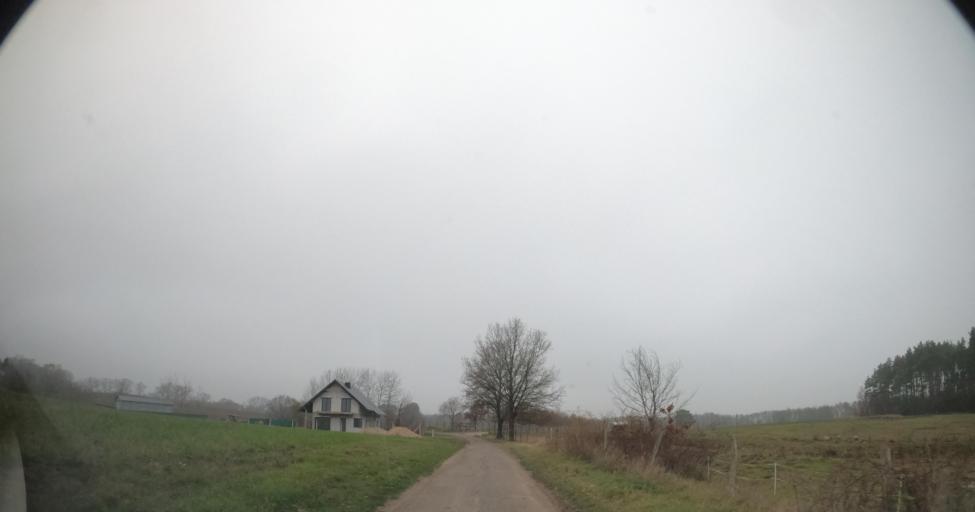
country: PL
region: West Pomeranian Voivodeship
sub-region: Powiat drawski
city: Drawsko Pomorskie
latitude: 53.5749
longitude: 15.8270
